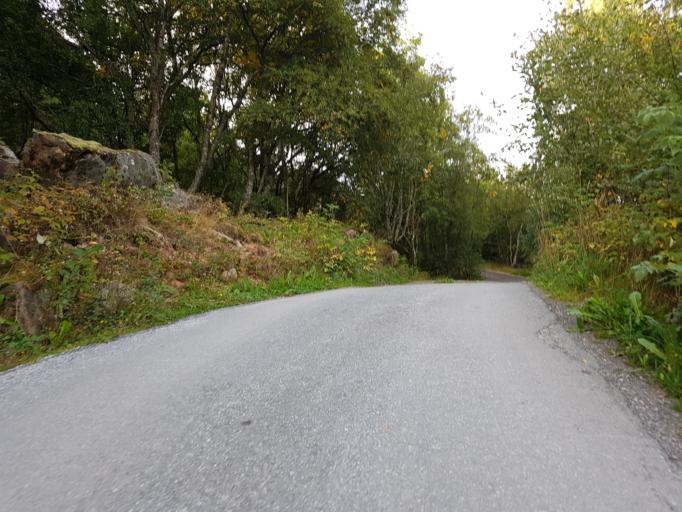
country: NO
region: Sor-Trondelag
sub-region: Afjord
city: A i Afjord
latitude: 64.0558
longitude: 9.9538
